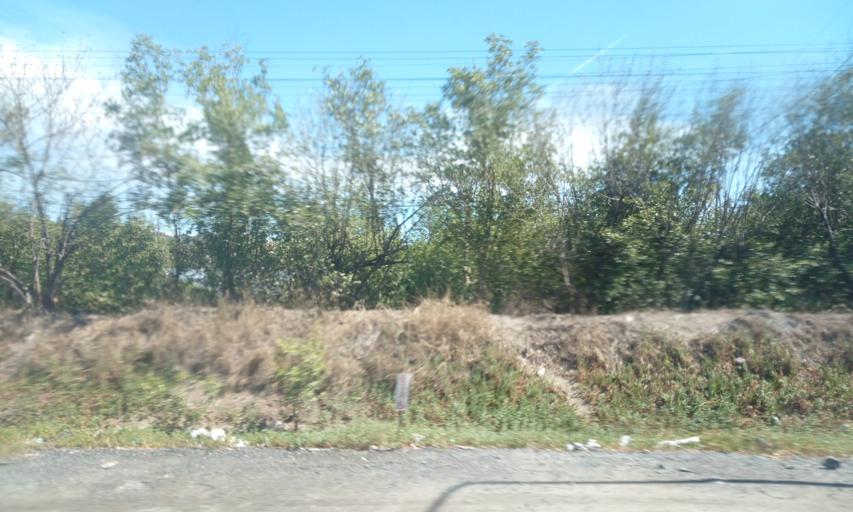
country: TH
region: Samut Prakan
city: Bang Bo District
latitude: 13.5017
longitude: 100.7655
